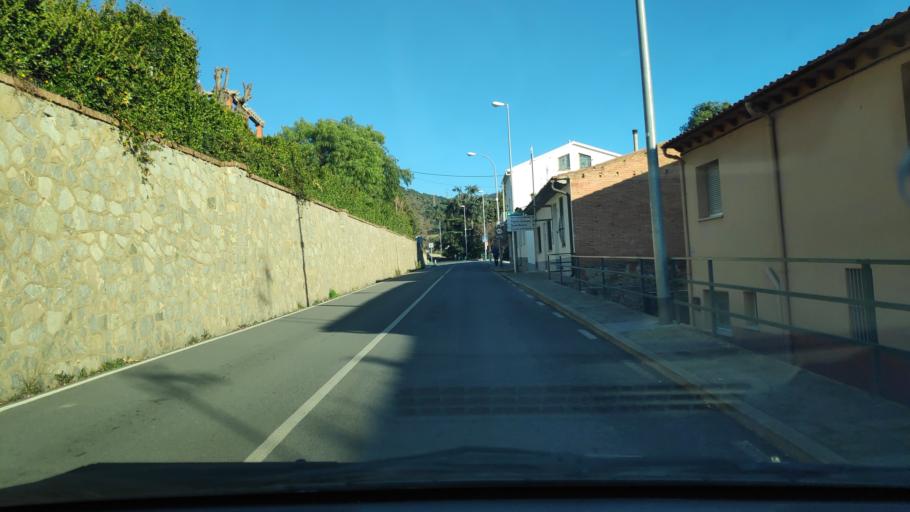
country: ES
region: Catalonia
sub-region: Provincia de Barcelona
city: Montmelo
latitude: 41.5278
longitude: 2.2377
